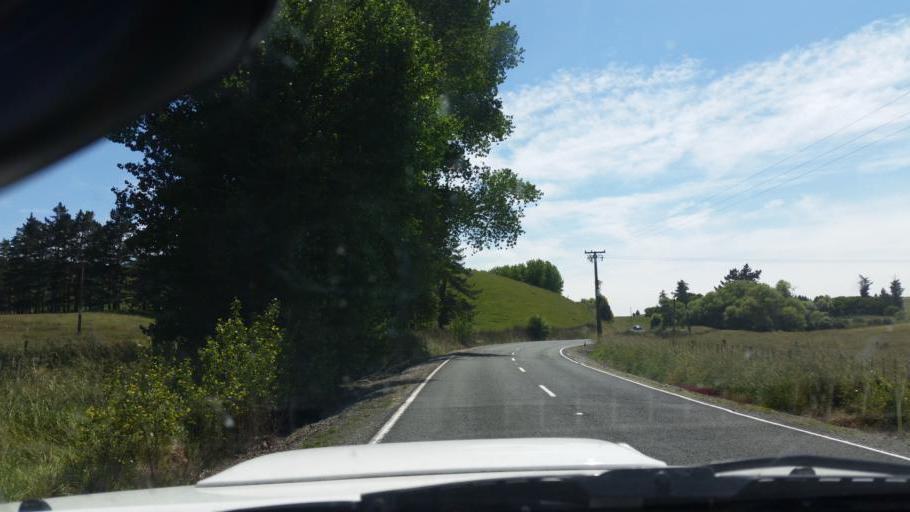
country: NZ
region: Auckland
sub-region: Auckland
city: Wellsford
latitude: -36.1906
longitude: 174.4046
